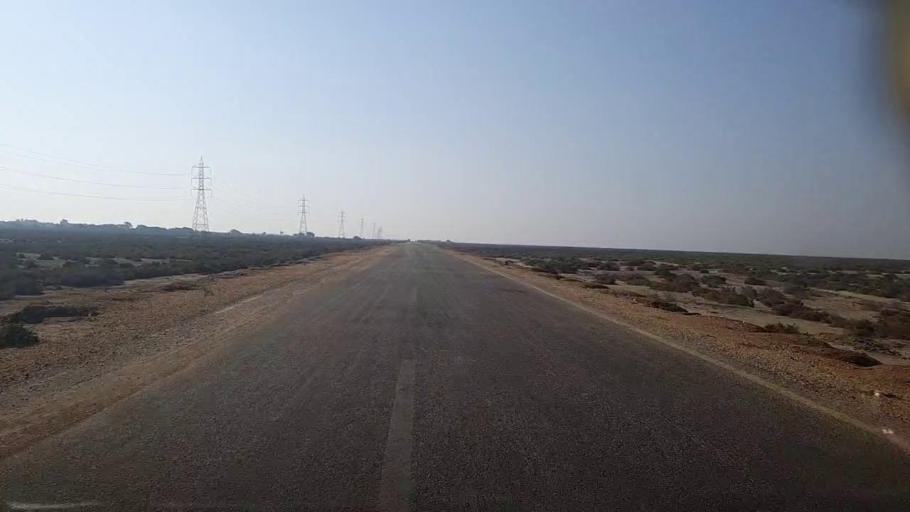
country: PK
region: Sindh
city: Gharo
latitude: 24.6267
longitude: 67.4969
